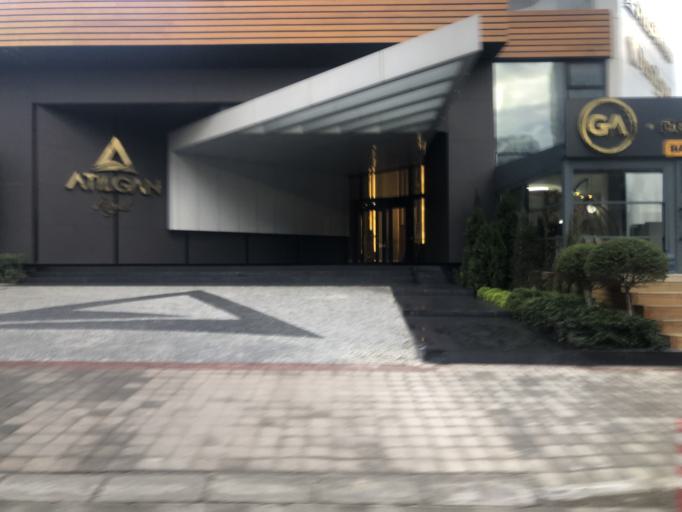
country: TR
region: Izmir
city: Karsiyaka
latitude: 38.4689
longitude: 27.0664
